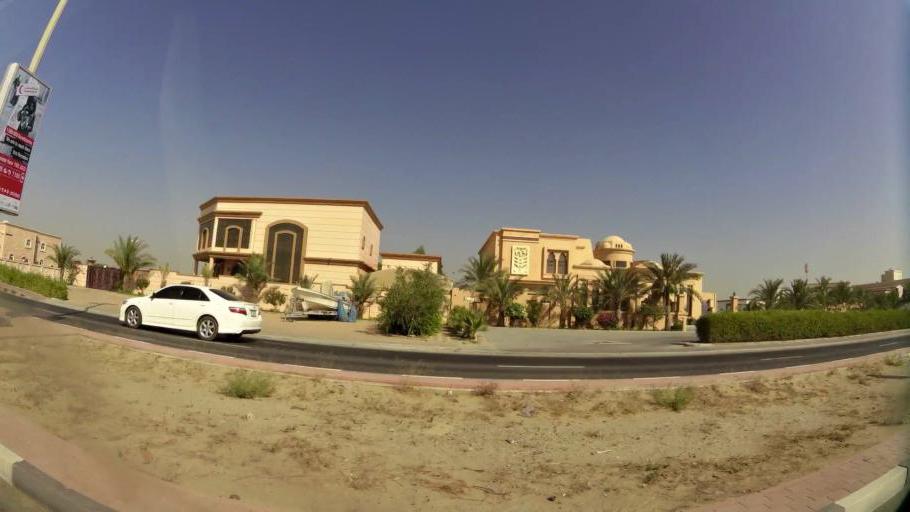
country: AE
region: Ajman
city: Ajman
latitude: 25.4197
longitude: 55.5144
